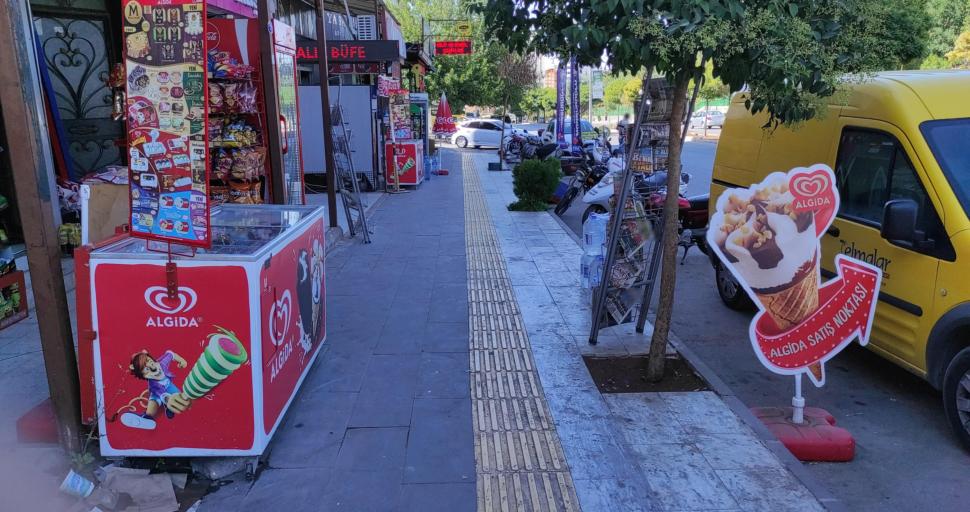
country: TR
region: Kilis
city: Kilis
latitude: 36.7283
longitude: 37.0999
